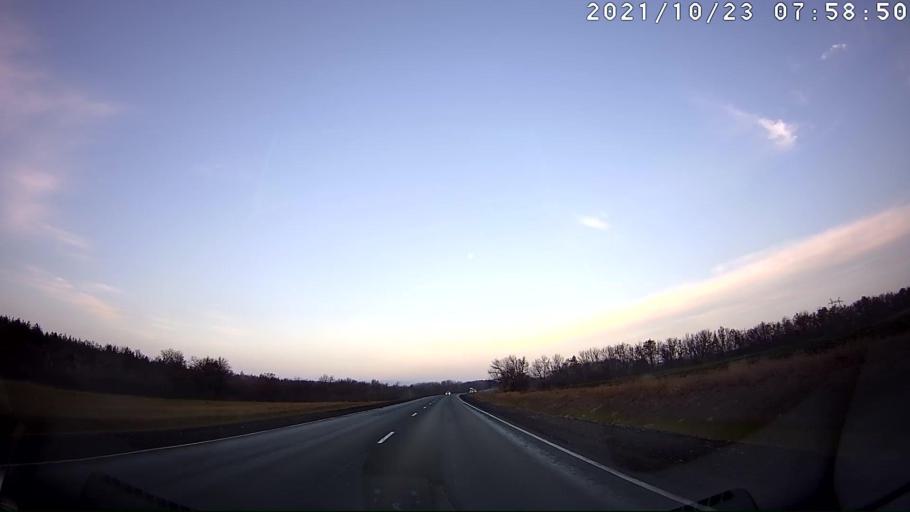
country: RU
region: Saratov
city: Tersa
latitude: 52.1019
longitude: 47.4622
